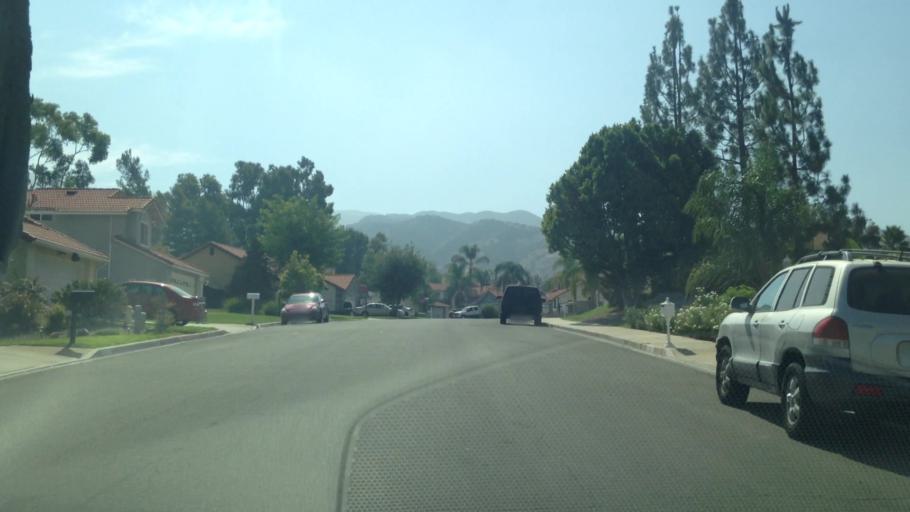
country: US
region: California
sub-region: Riverside County
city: El Cerrito
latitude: 33.7840
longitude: -117.4978
